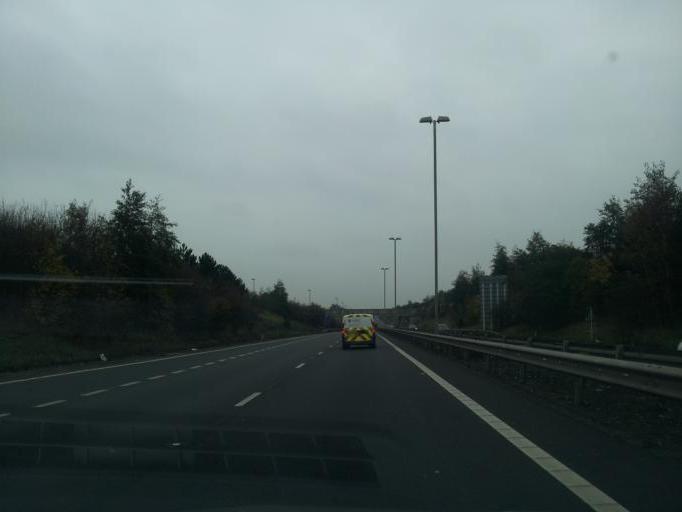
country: GB
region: England
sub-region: Bedford
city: Elstow
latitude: 52.1091
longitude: -0.4697
